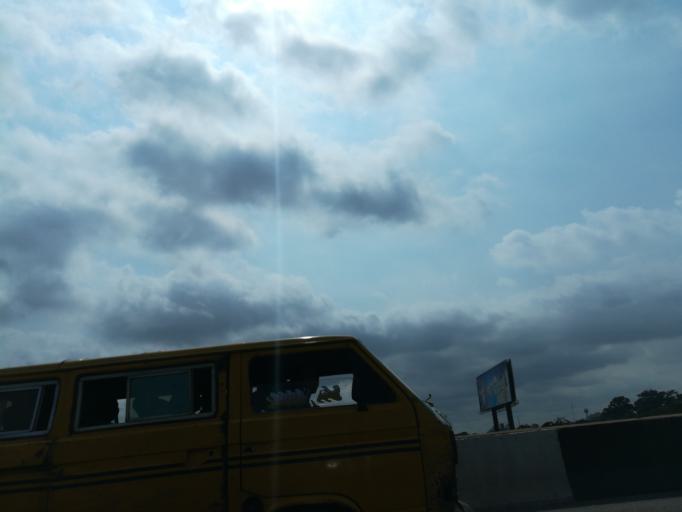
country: NG
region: Lagos
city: Makoko
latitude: 6.5150
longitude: 3.4056
